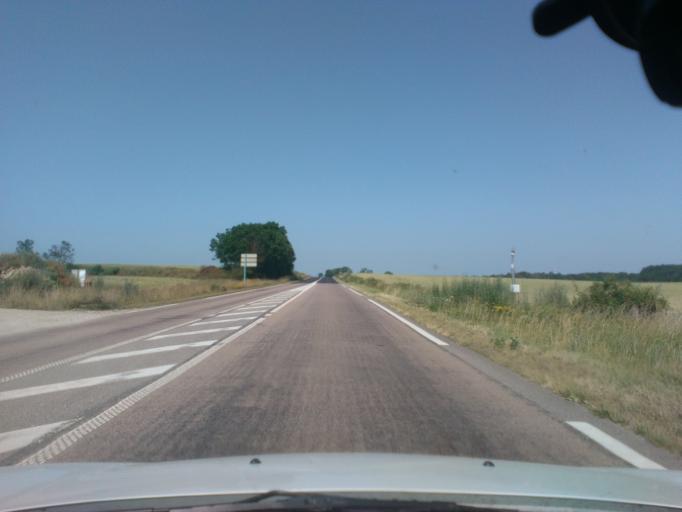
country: FR
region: Lorraine
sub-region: Departement des Vosges
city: Mirecourt
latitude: 48.3111
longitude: 6.0209
